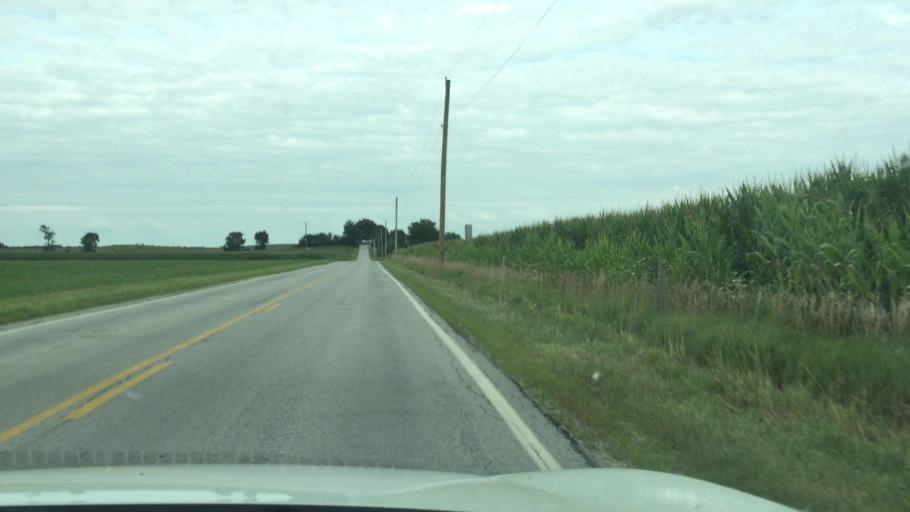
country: US
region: Ohio
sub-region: Clark County
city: Northridge
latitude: 39.9911
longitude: -83.6979
